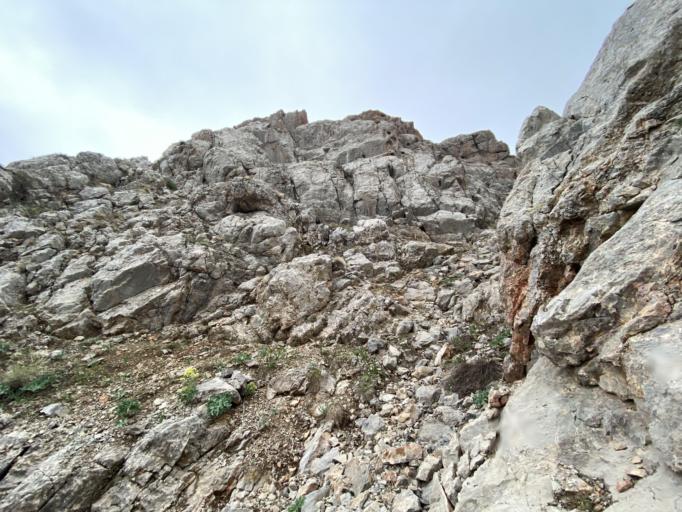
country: KZ
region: Ongtustik Qazaqstan
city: Ashchysay
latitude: 43.6272
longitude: 68.9590
